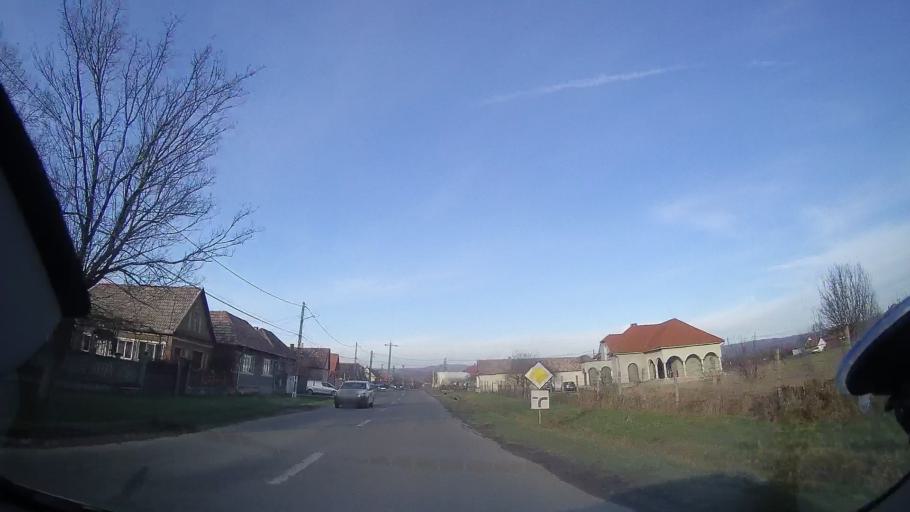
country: RO
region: Bihor
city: Lugasu de Jos
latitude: 47.0420
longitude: 22.3533
